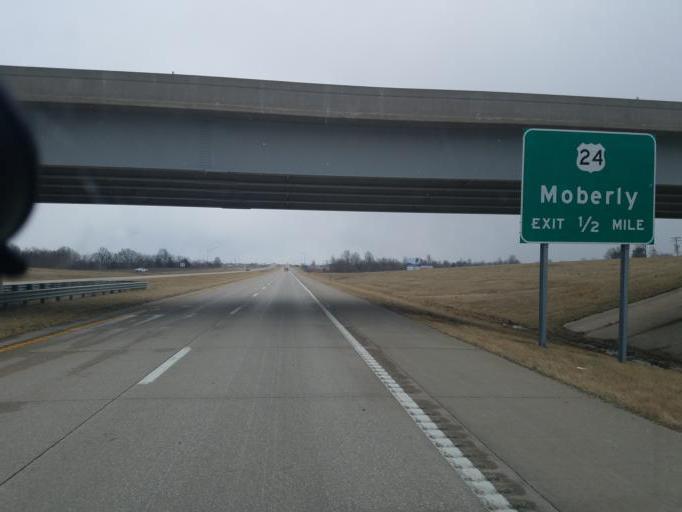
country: US
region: Missouri
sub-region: Randolph County
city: Moberly
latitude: 39.4549
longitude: -92.4320
